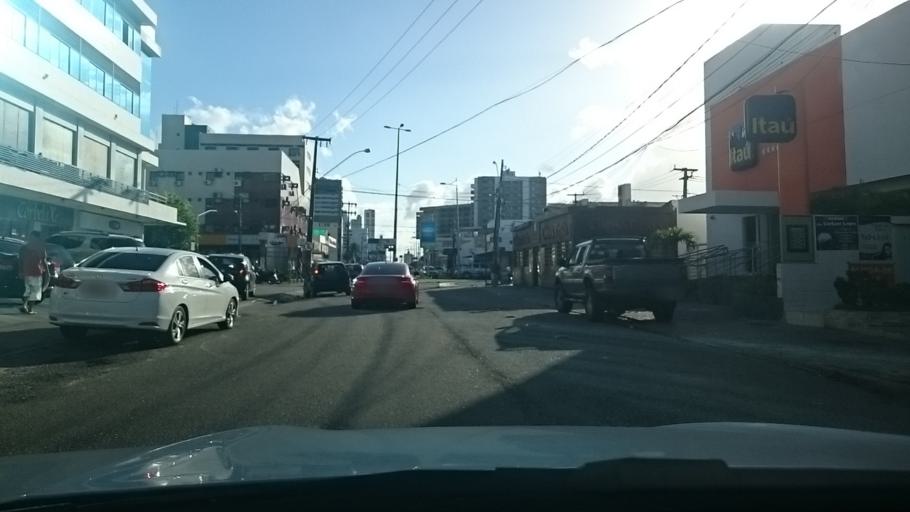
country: BR
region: Paraiba
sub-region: Joao Pessoa
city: Joao Pessoa
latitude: -7.0973
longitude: -34.8341
